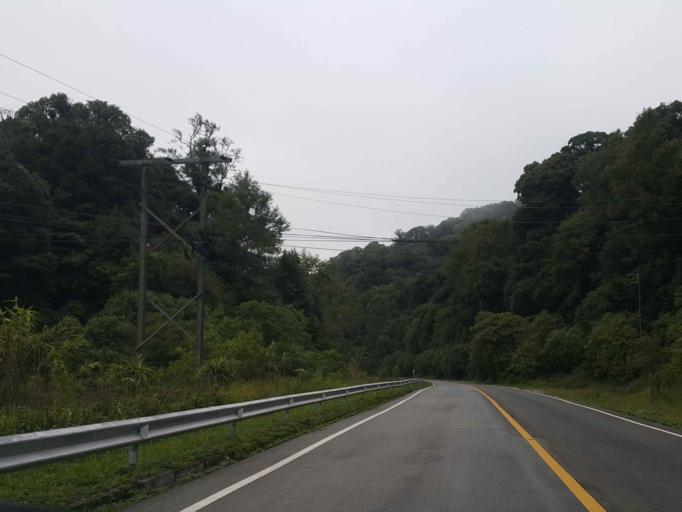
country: TH
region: Chiang Mai
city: Mae Chaem
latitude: 18.5632
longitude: 98.4843
